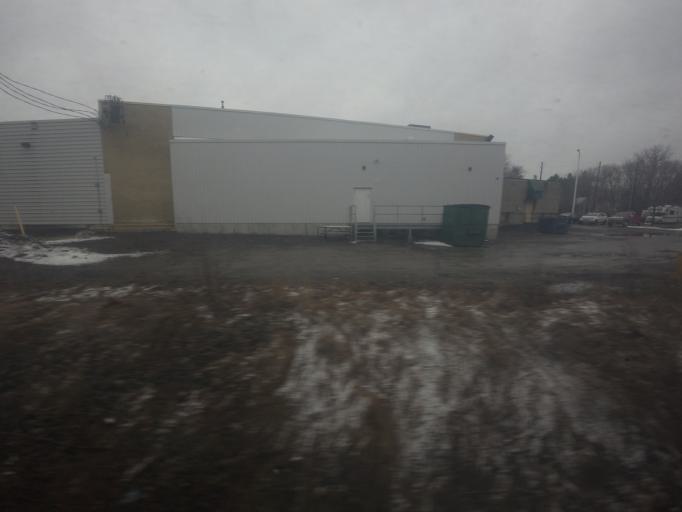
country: CA
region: Ontario
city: Brockville
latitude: 44.6006
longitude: -75.6912
